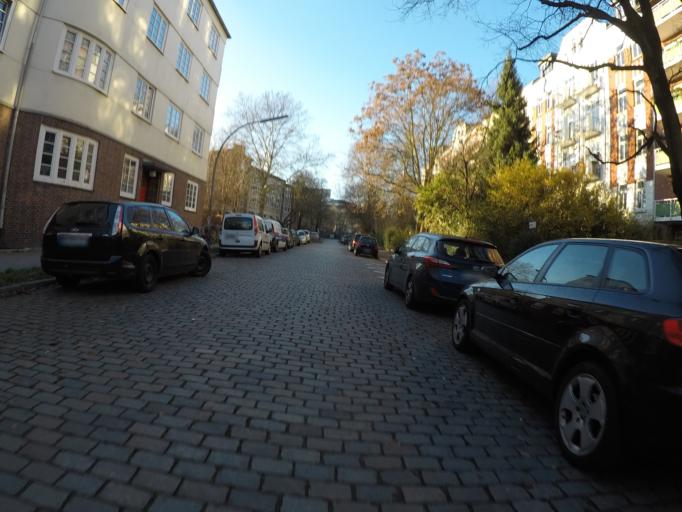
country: DE
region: Hamburg
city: St. Pauli
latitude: 53.5647
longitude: 9.9533
